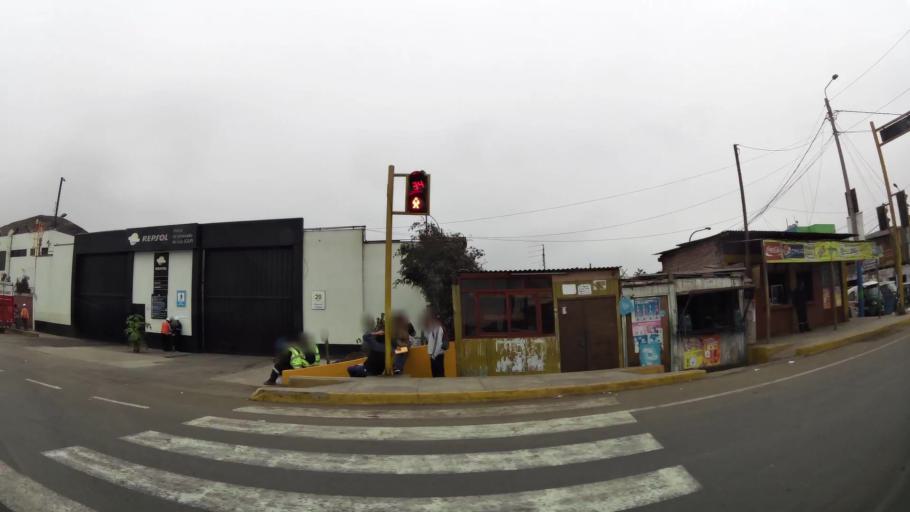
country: PE
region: Lima
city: Ventanilla
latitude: -11.9359
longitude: -77.1306
